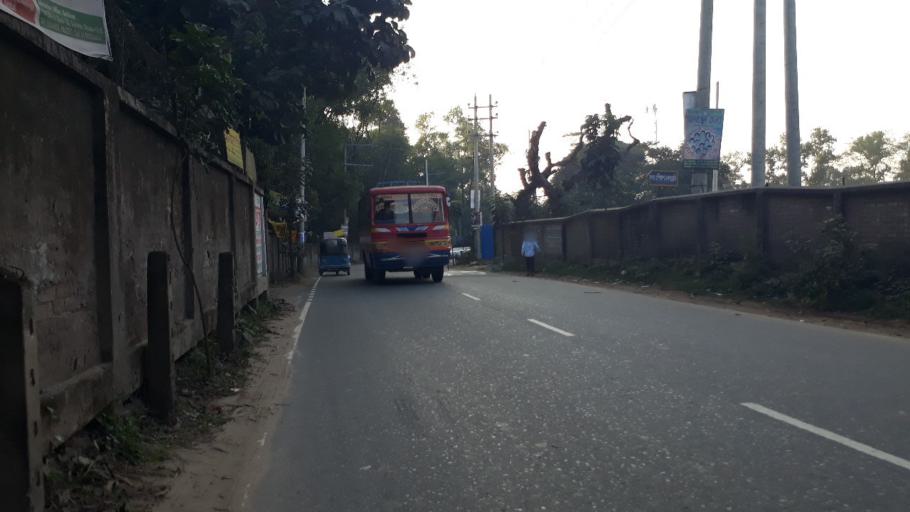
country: BD
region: Dhaka
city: Tungi
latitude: 23.8724
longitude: 90.2750
